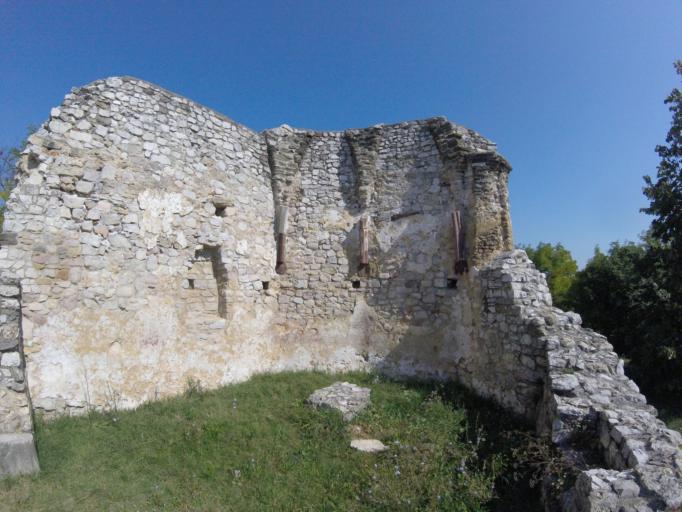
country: HU
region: Veszprem
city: Balatonfured
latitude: 46.9602
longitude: 17.8608
